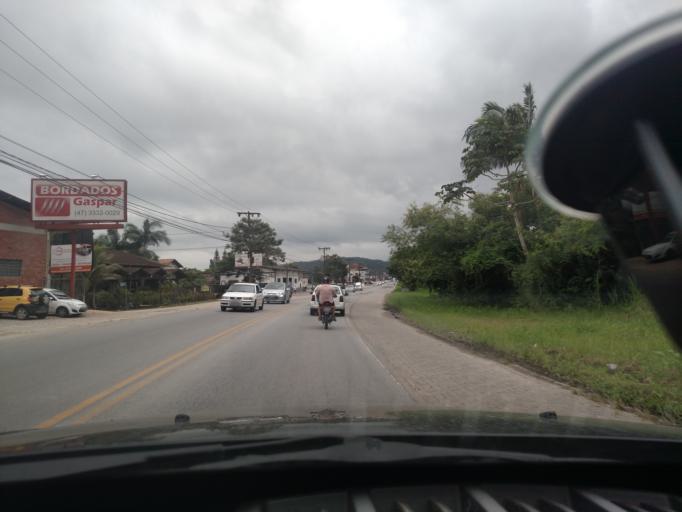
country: BR
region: Santa Catarina
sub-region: Gaspar
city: Gaspar
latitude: -26.9199
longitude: -48.9737
